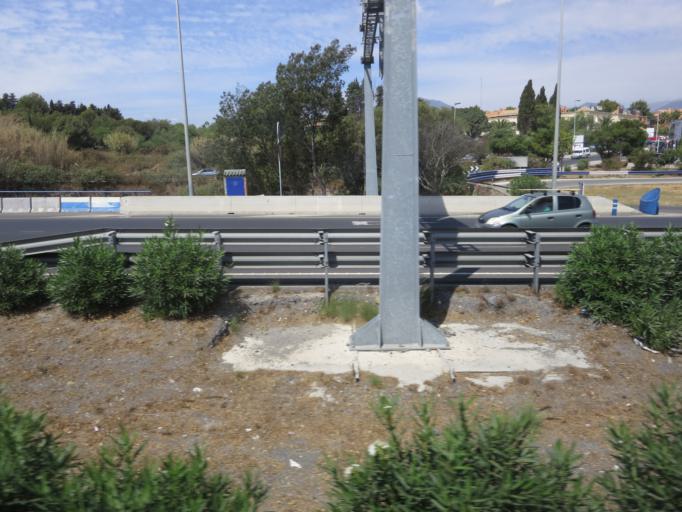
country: ES
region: Andalusia
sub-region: Provincia de Malaga
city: Marbella
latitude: 36.4934
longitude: -4.9518
